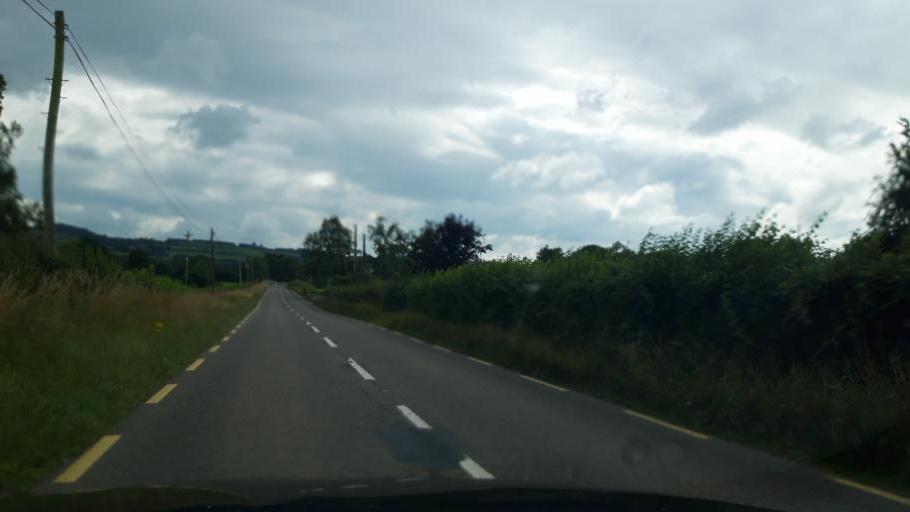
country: IE
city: Ballylinan
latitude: 52.9133
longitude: -7.0755
